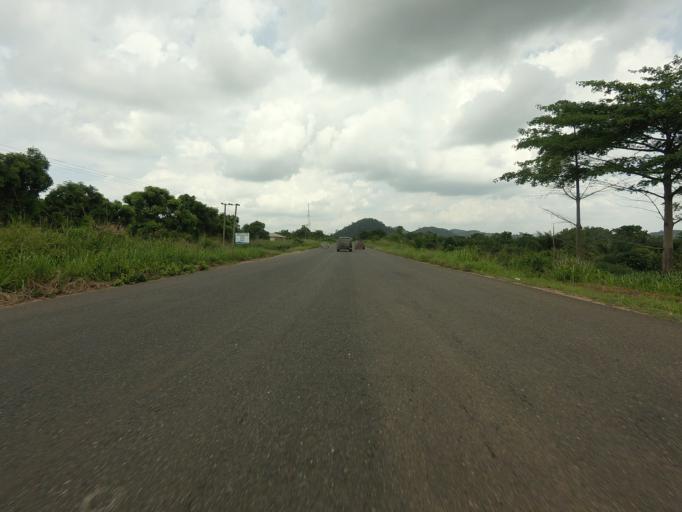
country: GH
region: Volta
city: Ho
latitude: 6.4350
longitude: 0.1706
